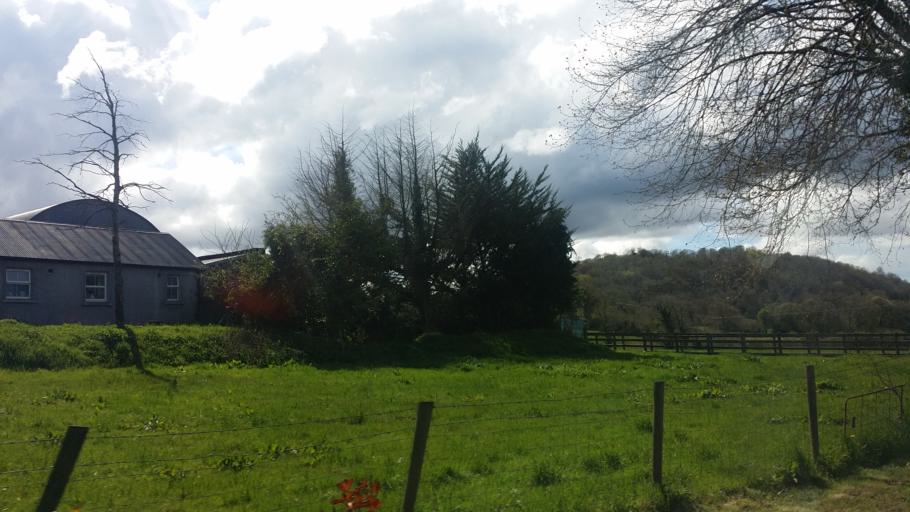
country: GB
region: Northern Ireland
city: Irvinestown
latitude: 54.4286
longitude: -7.7685
